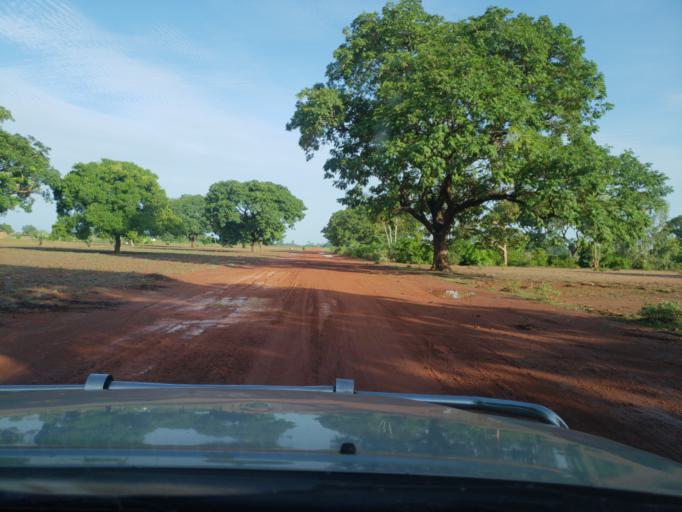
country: ML
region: Sikasso
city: Koutiala
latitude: 12.4282
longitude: -5.6027
